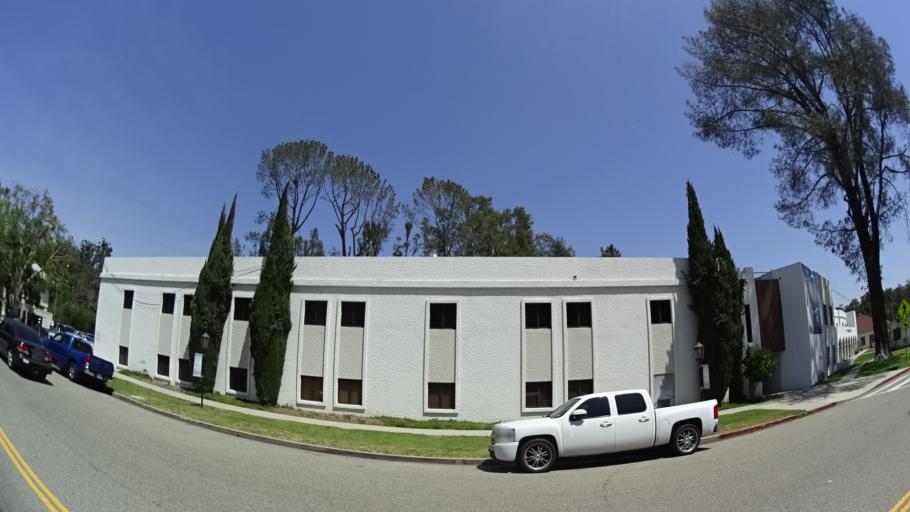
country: US
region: California
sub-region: Los Angeles County
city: Echo Park
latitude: 34.0761
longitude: -118.2487
